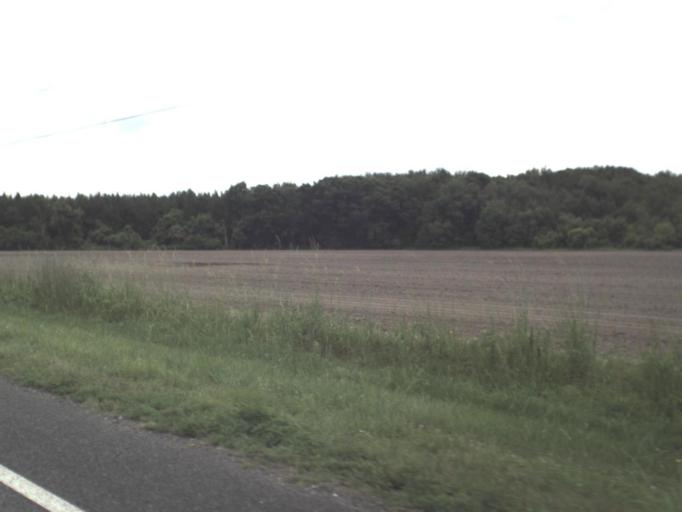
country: US
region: Florida
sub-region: Nassau County
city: Callahan
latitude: 30.6246
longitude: -81.8481
